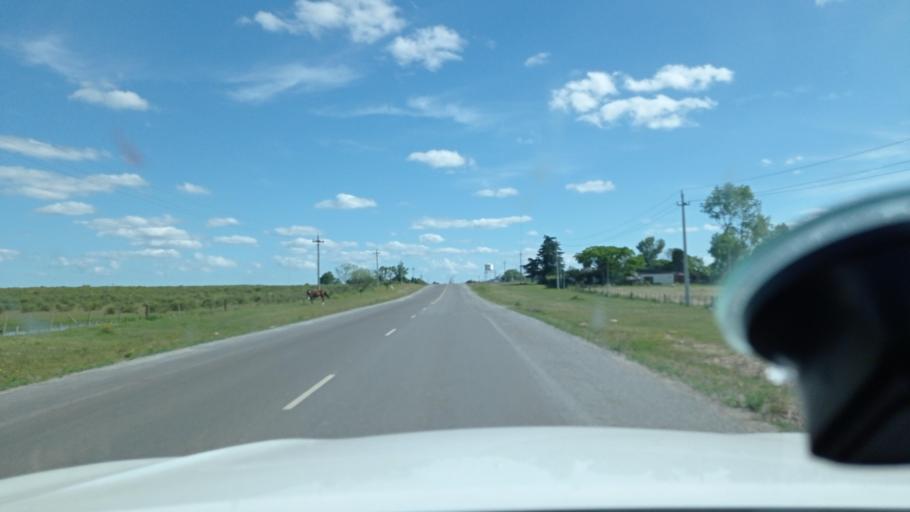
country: UY
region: Florida
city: Florida
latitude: -34.0820
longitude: -56.2360
